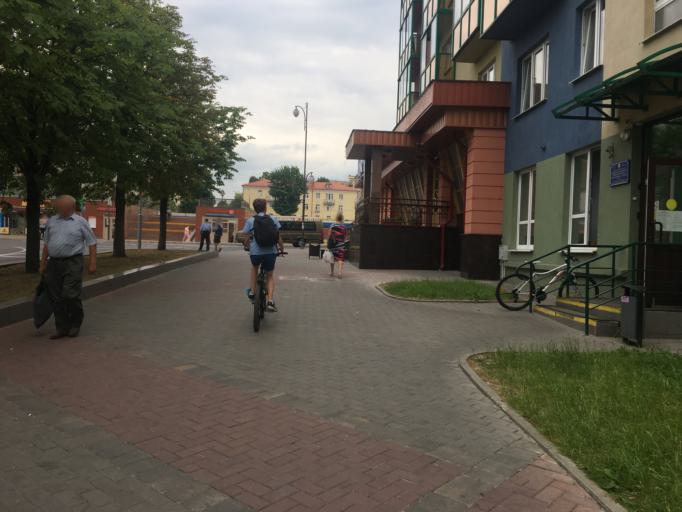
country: BY
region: Grodnenskaya
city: Hrodna
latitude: 53.6861
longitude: 23.8468
